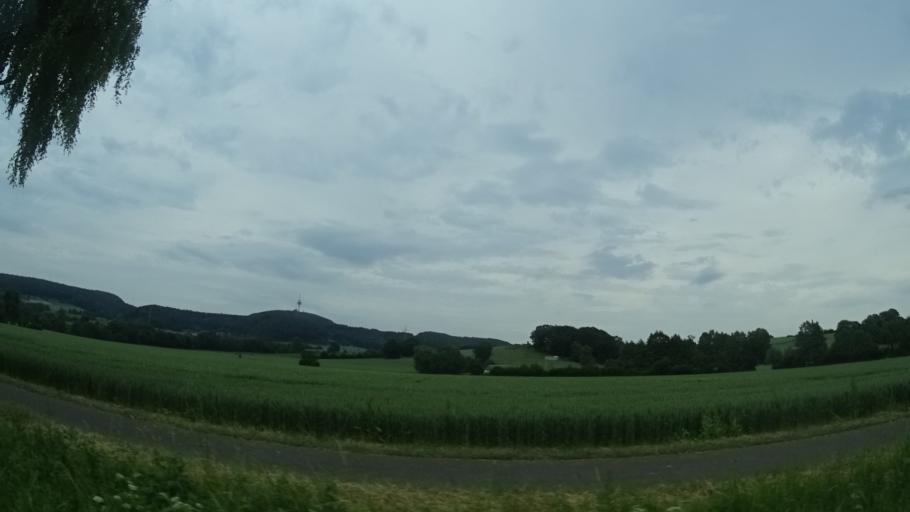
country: DE
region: Lower Saxony
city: Vahlbruch
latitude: 51.8496
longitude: 9.2856
